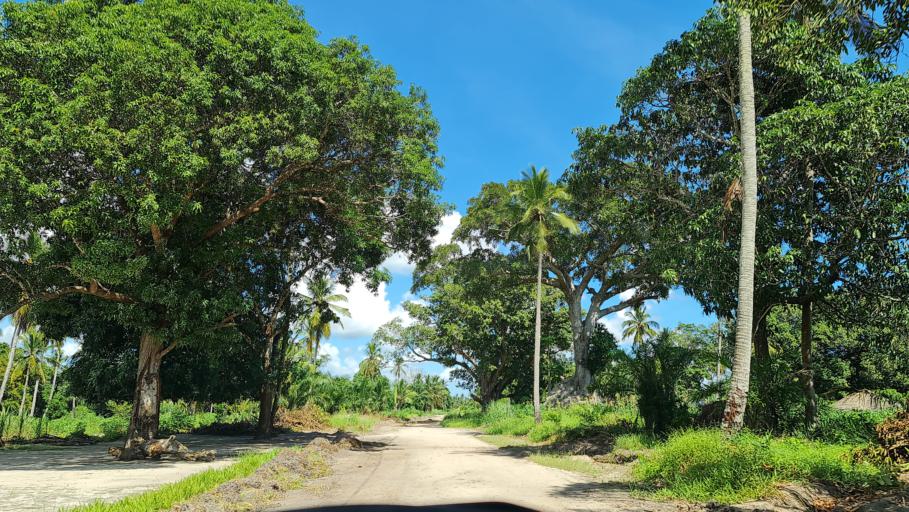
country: MZ
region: Zambezia
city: Quelimane
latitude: -17.3828
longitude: 37.5174
